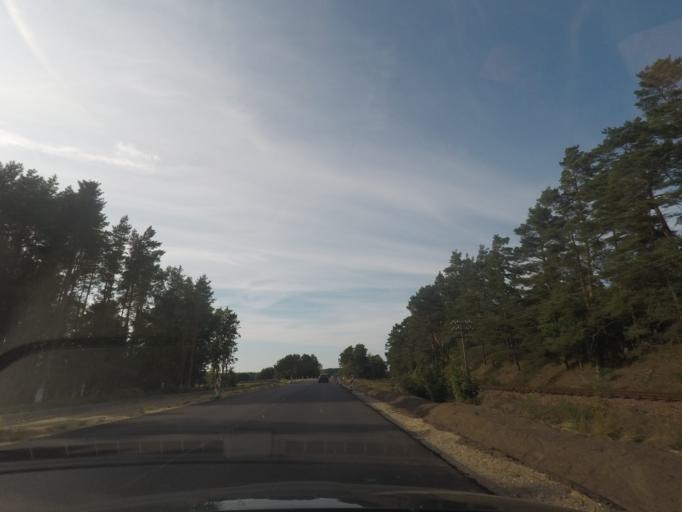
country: PL
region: Pomeranian Voivodeship
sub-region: Powiat leborski
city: Leba
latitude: 54.7239
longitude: 17.5709
